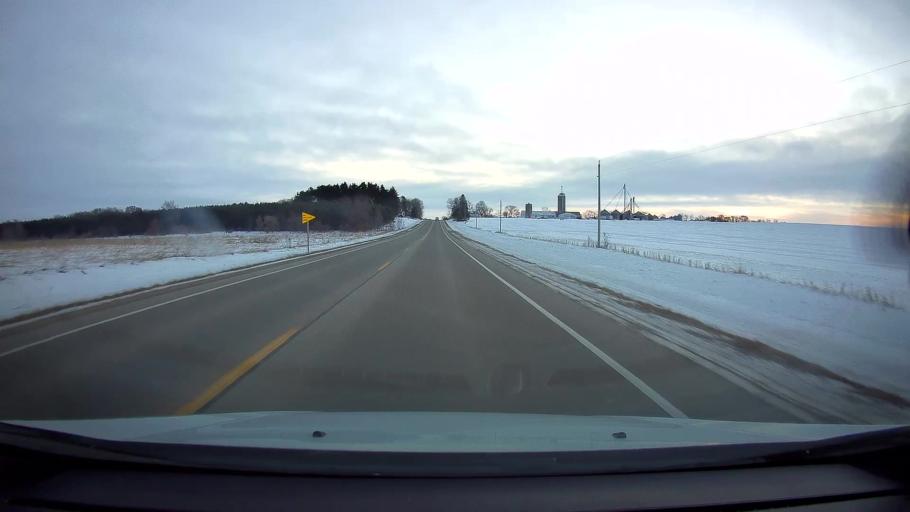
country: US
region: Wisconsin
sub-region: Saint Croix County
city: New Richmond
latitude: 45.1371
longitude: -92.4852
